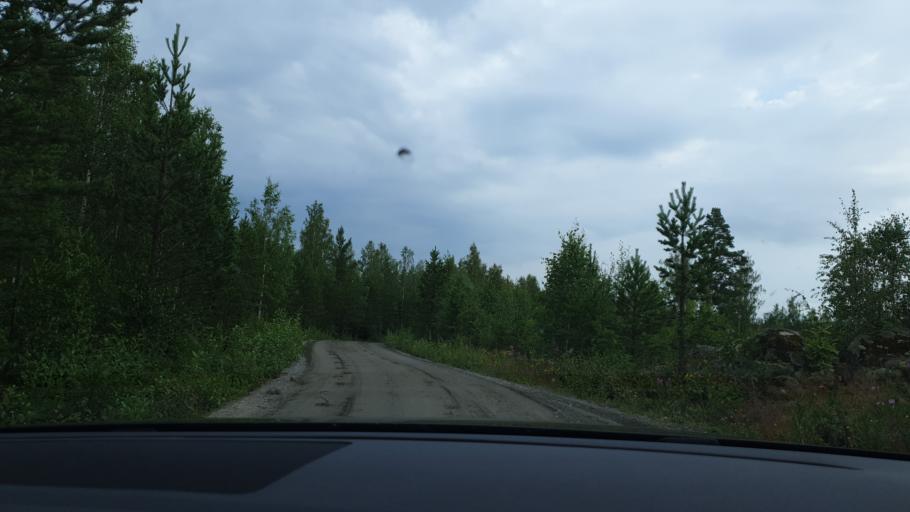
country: SE
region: Gaevleborg
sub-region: Hudiksvalls Kommun
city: Iggesund
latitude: 61.5136
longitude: 17.0169
